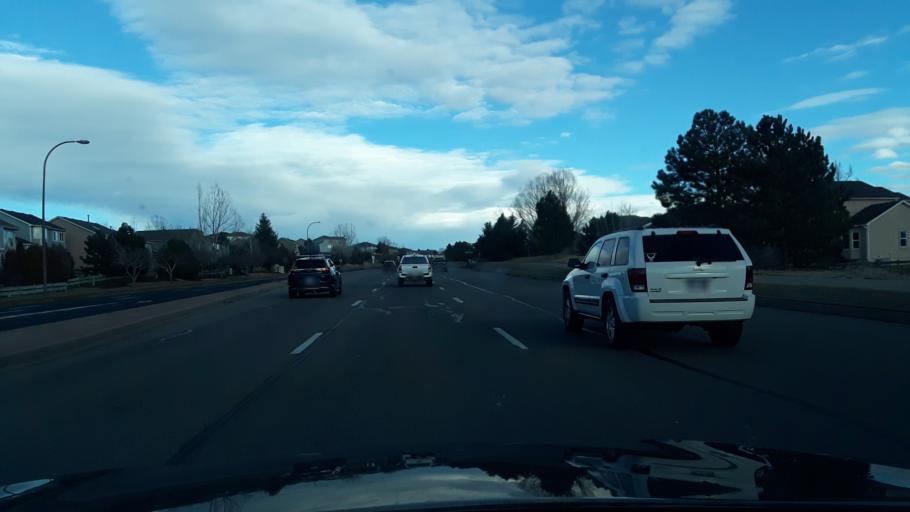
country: US
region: Colorado
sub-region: El Paso County
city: Gleneagle
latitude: 39.0082
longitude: -104.8034
